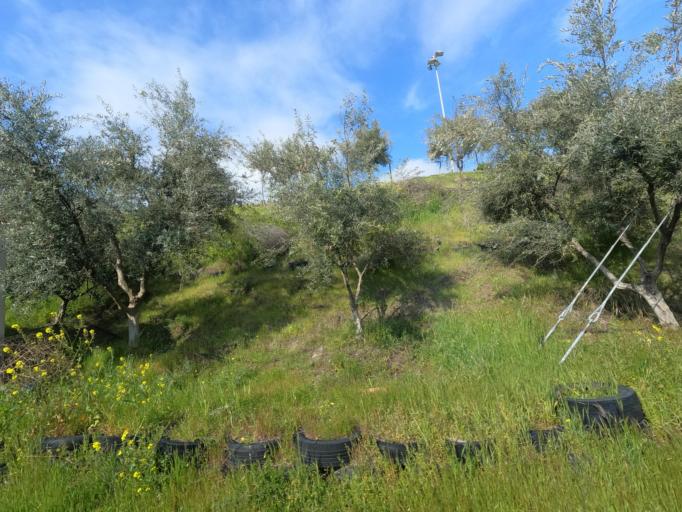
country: CY
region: Lefkosia
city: Astromeritis
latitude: 35.0828
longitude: 32.9538
